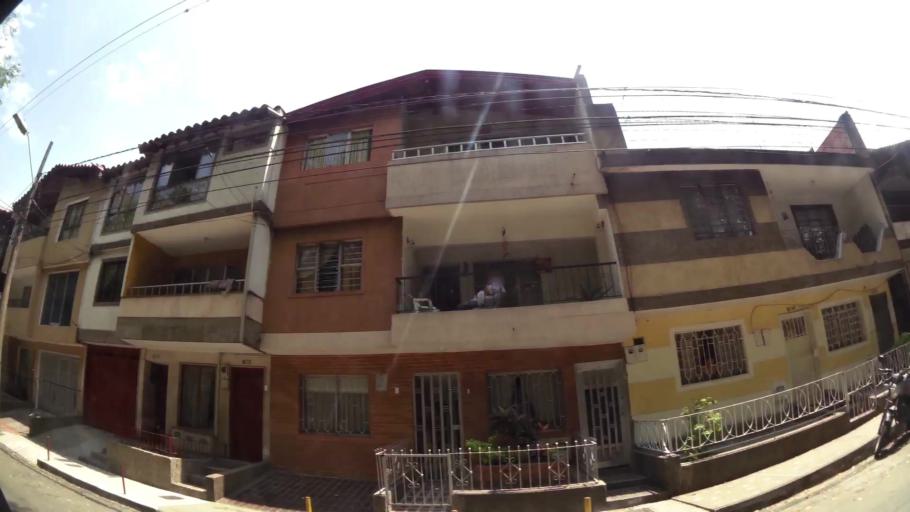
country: CO
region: Antioquia
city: Itagui
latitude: 6.2251
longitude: -75.6036
